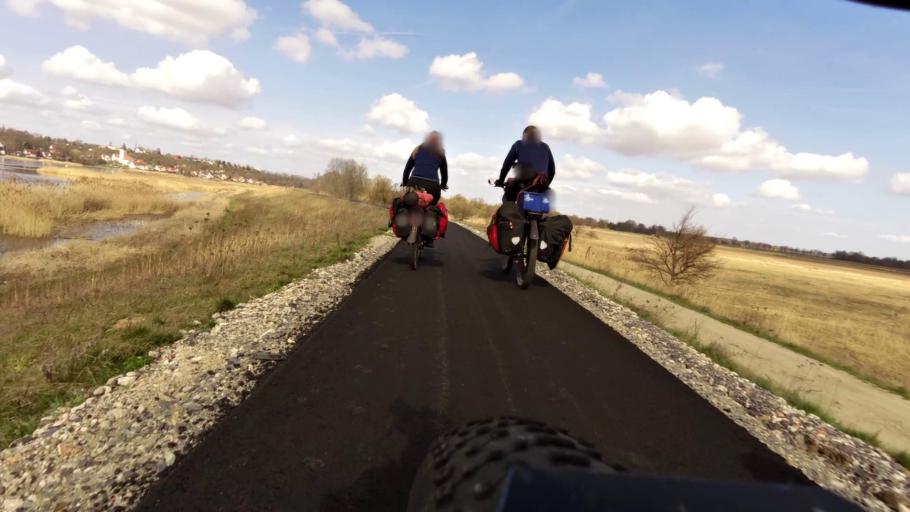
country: DE
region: Brandenburg
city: Lebus
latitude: 52.4179
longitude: 14.5487
